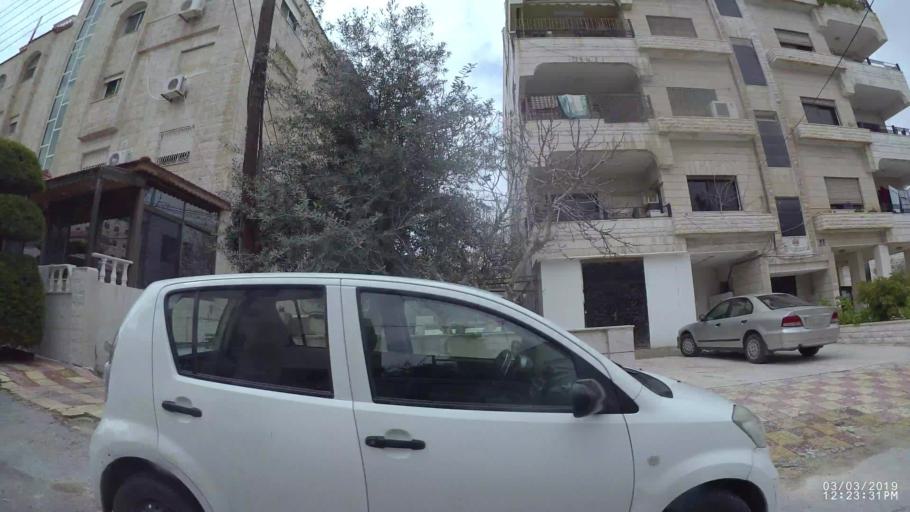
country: JO
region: Amman
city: Amman
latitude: 31.9776
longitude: 35.9003
